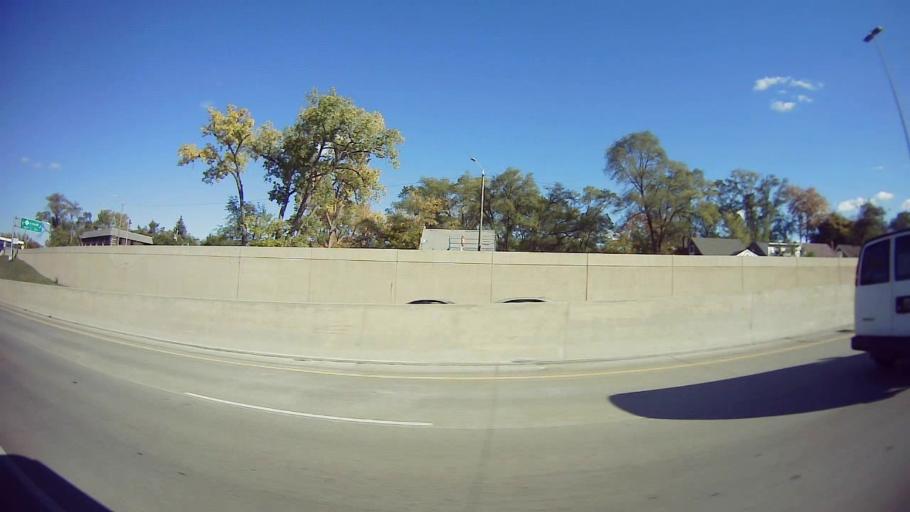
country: US
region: Michigan
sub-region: Oakland County
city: Southfield
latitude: 42.4423
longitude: -83.2199
